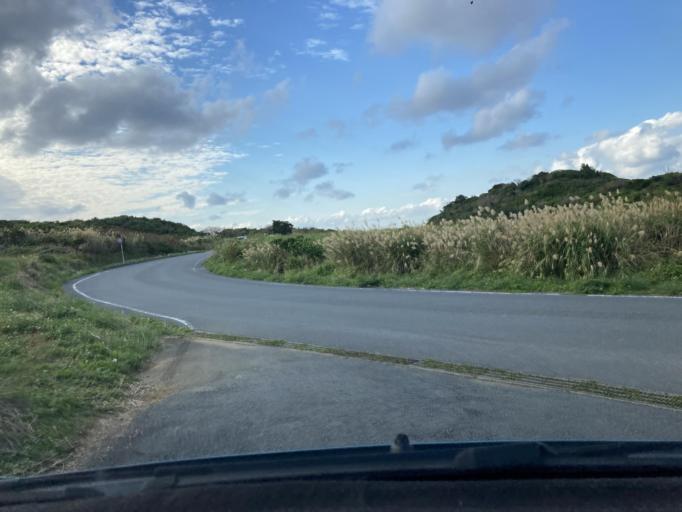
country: JP
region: Okinawa
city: Nago
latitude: 26.8669
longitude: 128.2601
